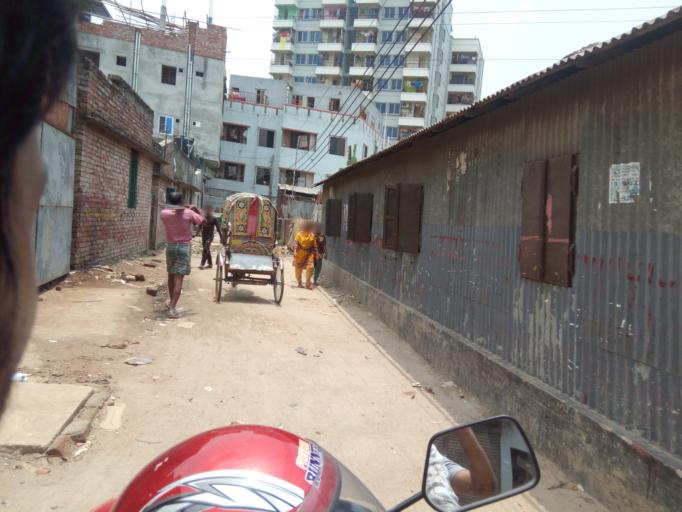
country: BD
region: Dhaka
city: Paltan
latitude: 23.7675
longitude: 90.4308
